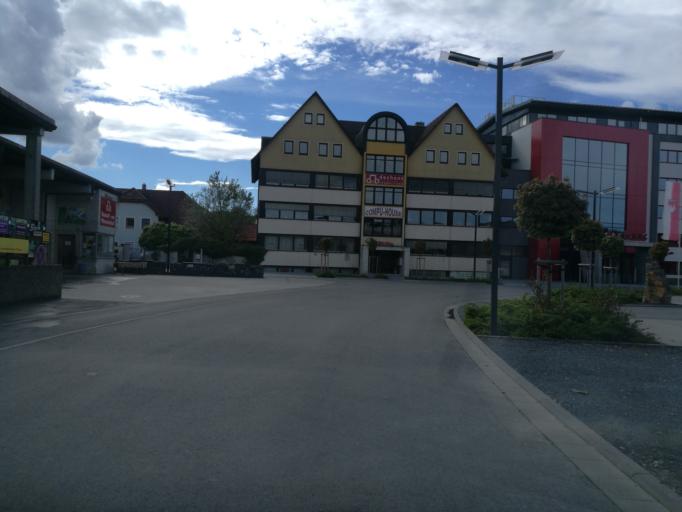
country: DE
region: Bavaria
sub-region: Upper Franconia
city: Weismain
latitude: 50.0869
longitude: 11.2412
